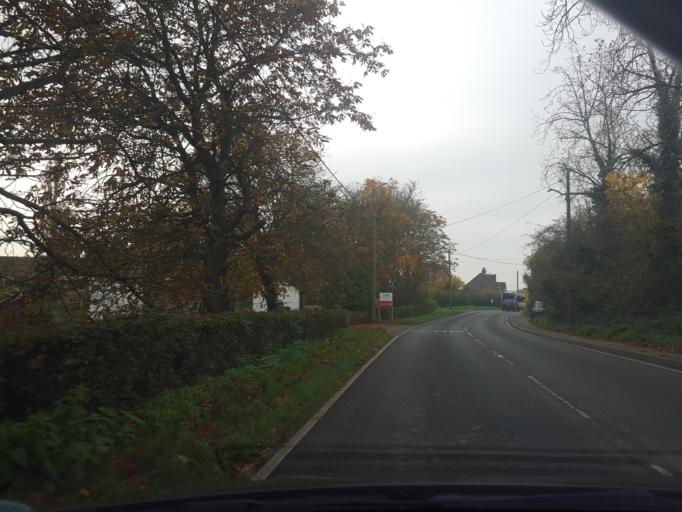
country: GB
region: England
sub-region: Essex
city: Little Clacton
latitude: 51.8191
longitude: 1.1294
